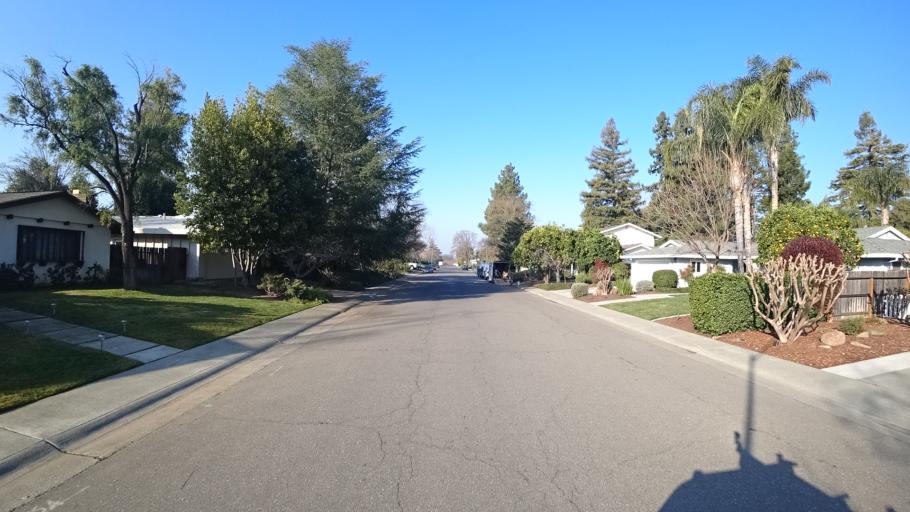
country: US
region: California
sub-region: Yolo County
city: Davis
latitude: 38.5474
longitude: -121.7907
